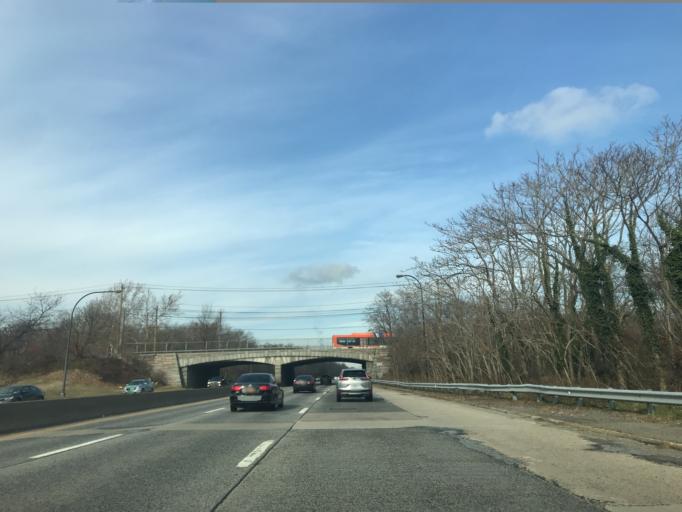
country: US
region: New York
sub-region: Nassau County
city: North Merrick
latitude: 40.6935
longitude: -73.5756
